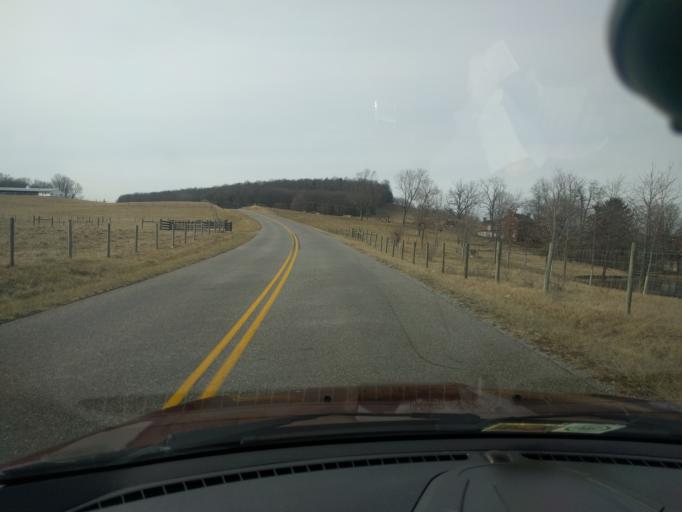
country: US
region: Virginia
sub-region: Augusta County
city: Stuarts Draft
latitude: 37.9305
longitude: -79.2128
